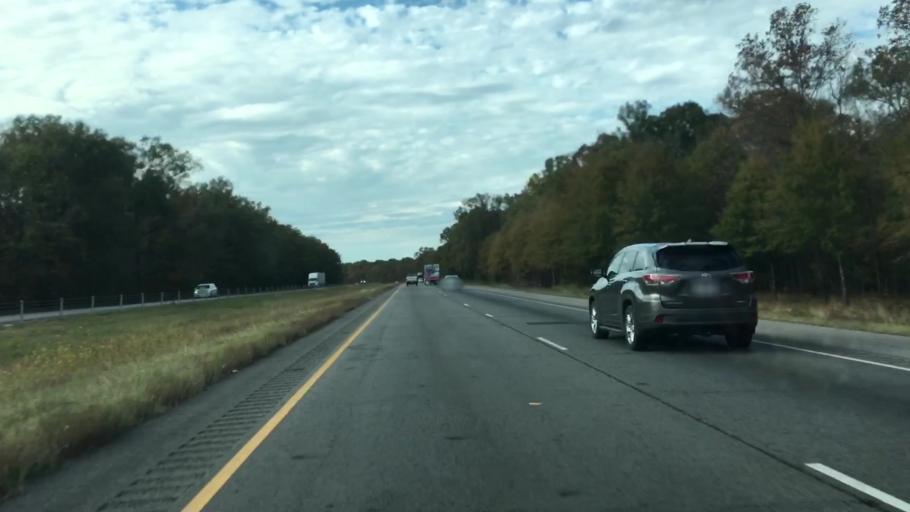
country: US
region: Arkansas
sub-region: Pope County
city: Atkins
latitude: 35.2413
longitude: -92.8594
